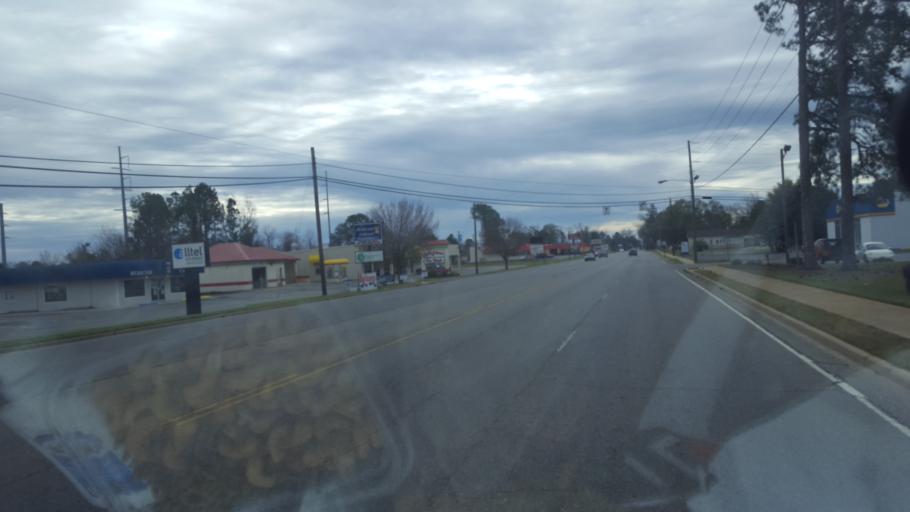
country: US
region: Georgia
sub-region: Irwin County
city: Ocilla
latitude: 31.6034
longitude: -83.2504
